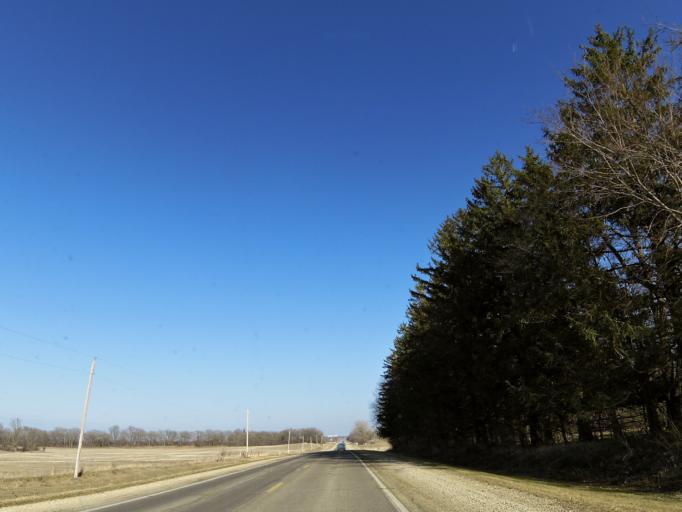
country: US
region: Iowa
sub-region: Worth County
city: Northwood
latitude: 43.4443
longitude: -93.2723
